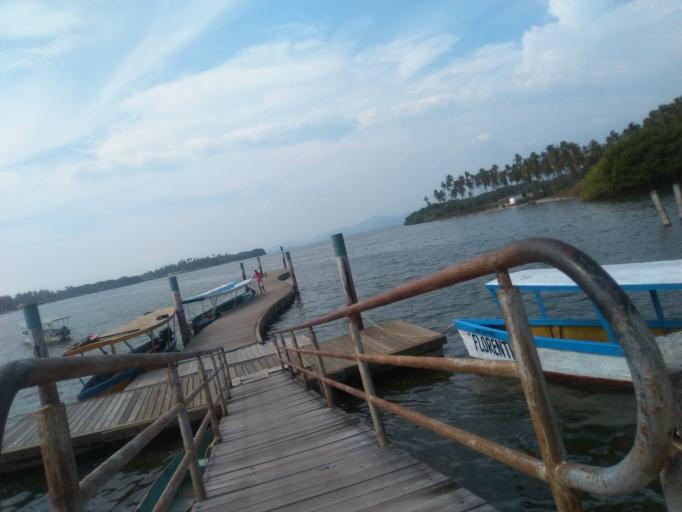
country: MX
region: Guerrero
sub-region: Coyuca de Benitez
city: Colonia Luces en el Mar
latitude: 16.9012
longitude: -99.9679
